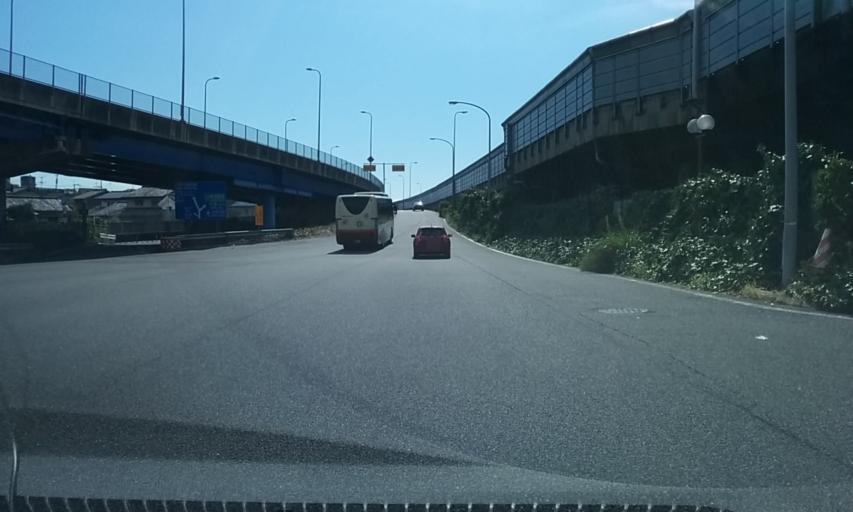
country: JP
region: Osaka
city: Ikeda
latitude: 34.8049
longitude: 135.4329
